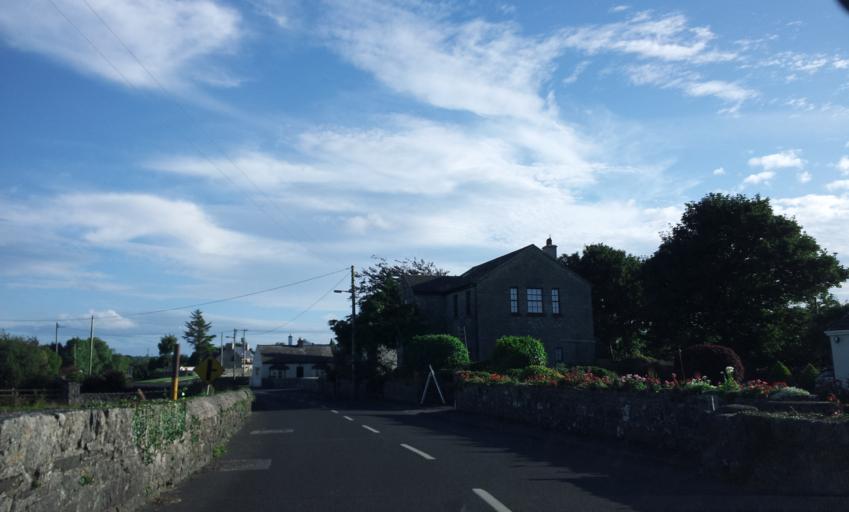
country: IE
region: Munster
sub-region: An Clar
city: Ennis
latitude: 52.9434
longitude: -9.0622
